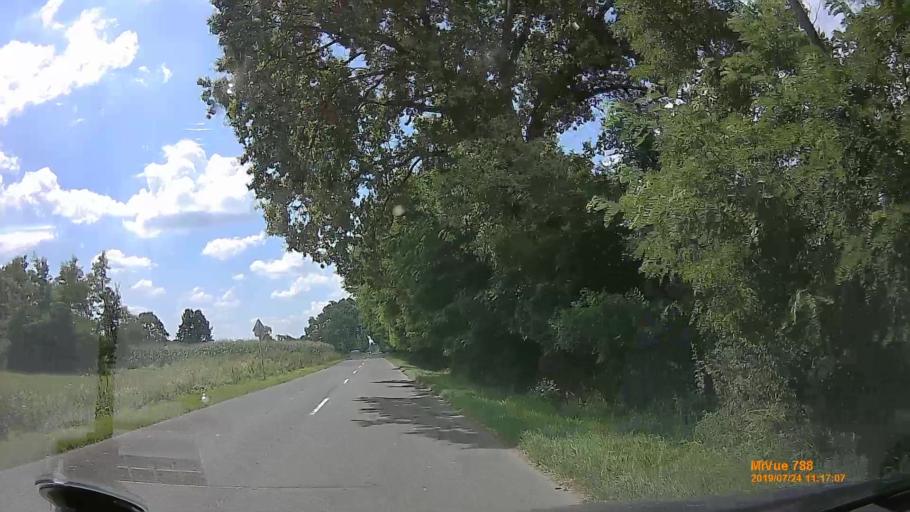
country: HU
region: Szabolcs-Szatmar-Bereg
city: Tarpa
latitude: 48.1733
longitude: 22.4617
